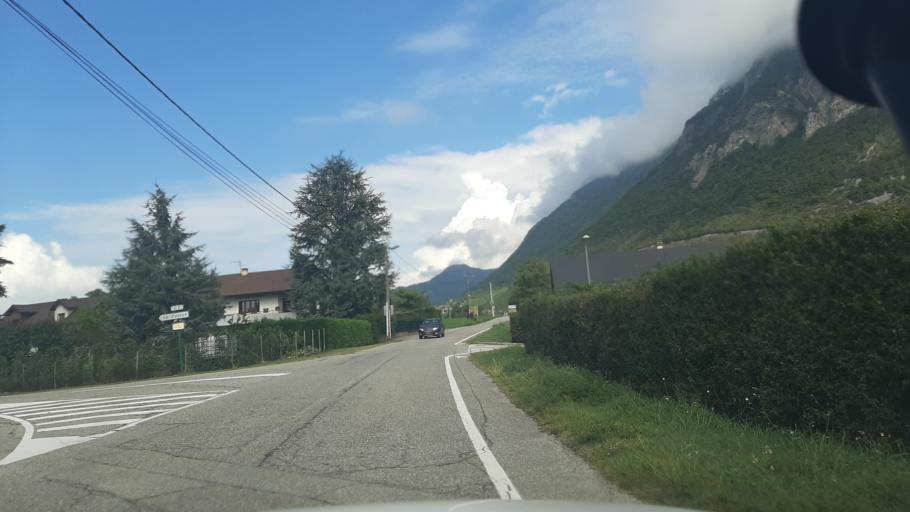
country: FR
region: Rhone-Alpes
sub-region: Departement de la Savoie
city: Montmelian
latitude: 45.5024
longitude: 6.0266
